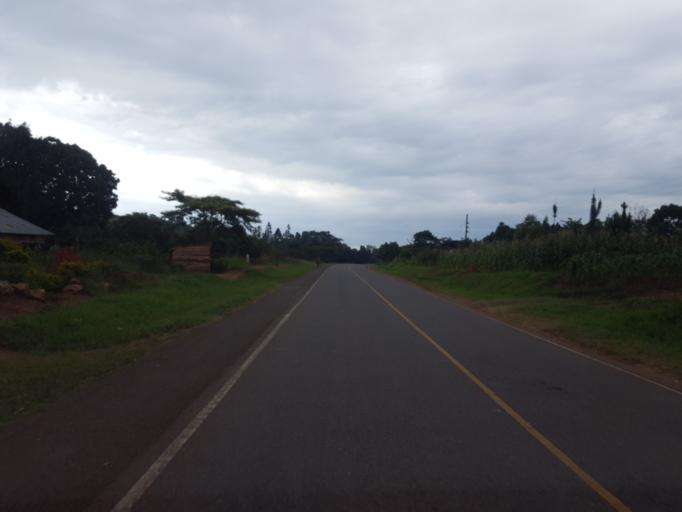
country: UG
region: Central Region
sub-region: Kiboga District
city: Kiboga
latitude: 0.9745
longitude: 31.7338
